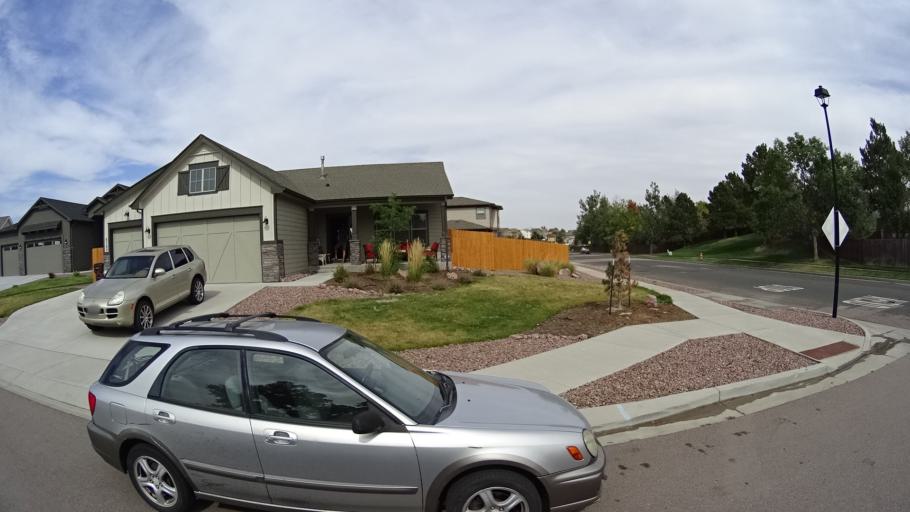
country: US
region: Colorado
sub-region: El Paso County
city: Cimarron Hills
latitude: 38.9033
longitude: -104.7021
